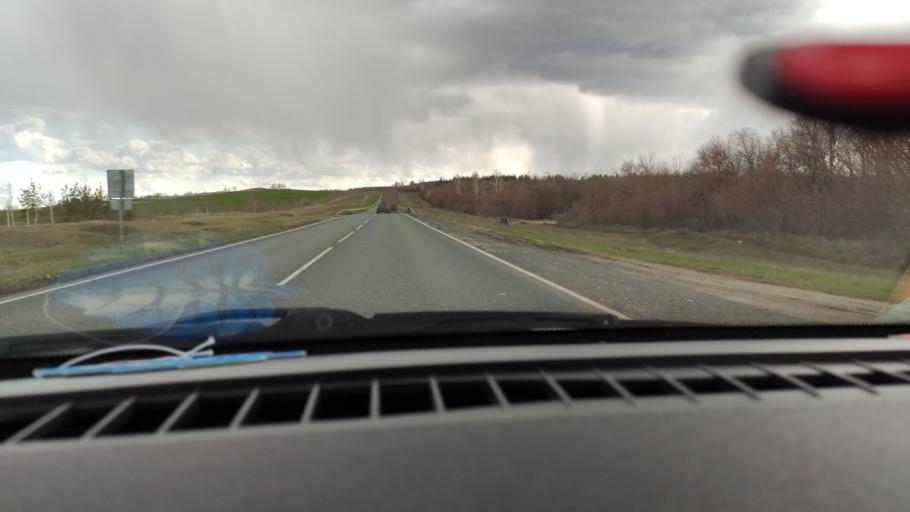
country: RU
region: Saratov
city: Balakovo
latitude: 52.1725
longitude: 47.8324
